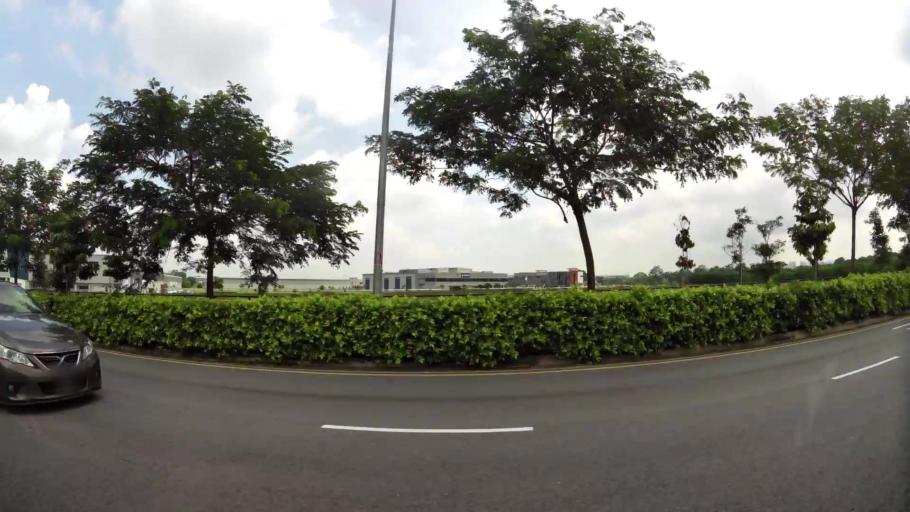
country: MY
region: Johor
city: Kampung Pasir Gudang Baru
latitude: 1.4026
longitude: 103.8550
